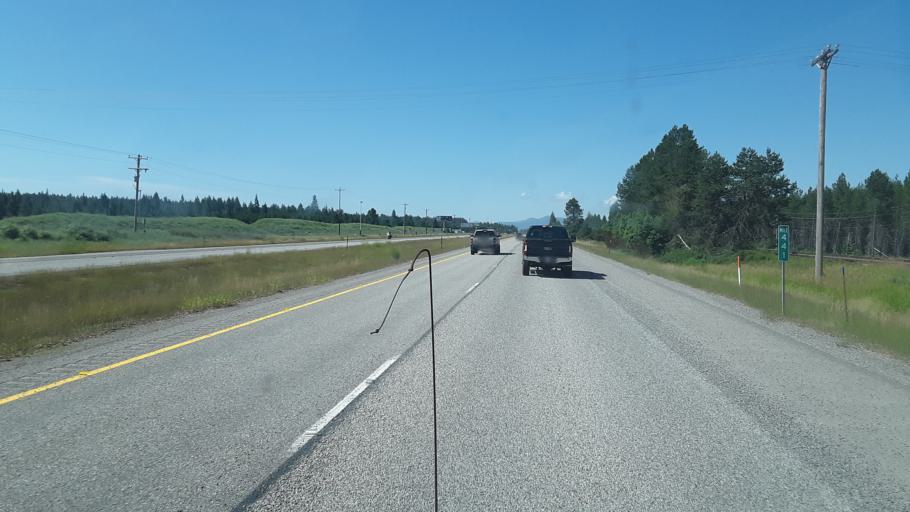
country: US
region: Idaho
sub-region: Kootenai County
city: Hayden
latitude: 47.8435
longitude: -116.7663
